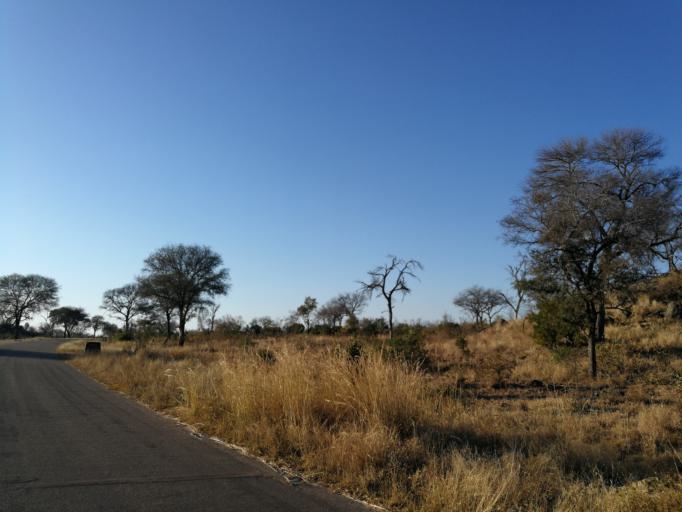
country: ZA
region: Limpopo
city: Thulamahashi
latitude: -25.0153
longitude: 31.4273
